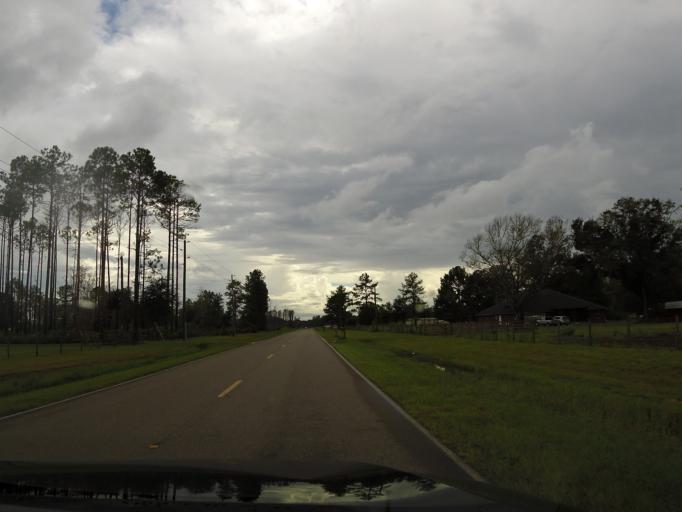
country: US
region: Florida
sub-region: Duval County
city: Baldwin
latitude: 30.4182
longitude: -82.0263
